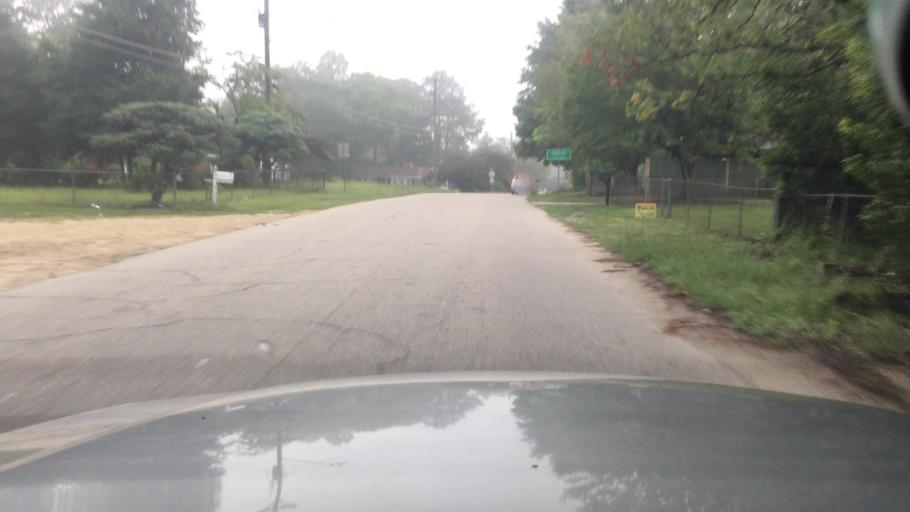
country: US
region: North Carolina
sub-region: Cumberland County
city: Hope Mills
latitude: 35.0174
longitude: -78.9273
